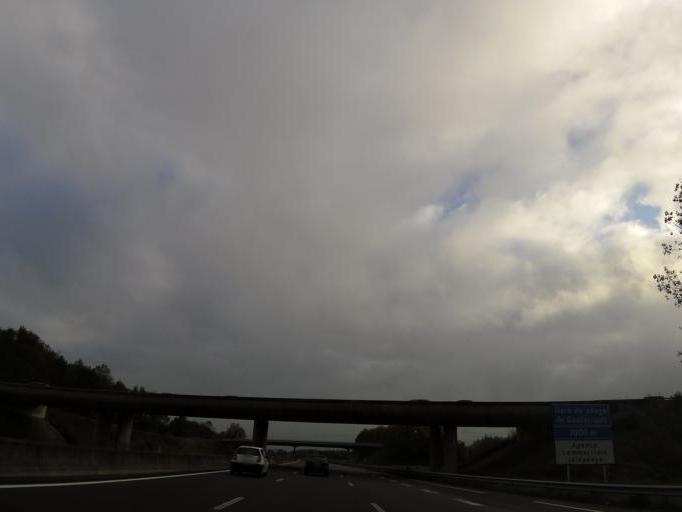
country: FR
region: Ile-de-France
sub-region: Departement de Seine-et-Marne
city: Bailly-Romainvilliers
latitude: 48.8404
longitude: 2.8213
